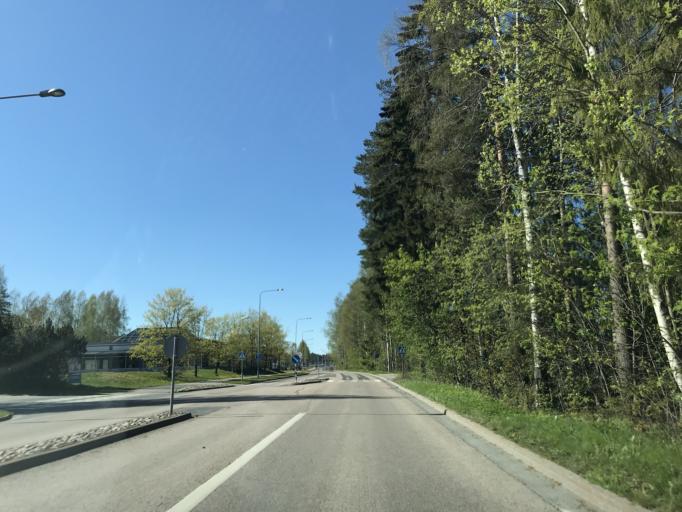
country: FI
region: Uusimaa
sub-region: Helsinki
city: Hyvinge
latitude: 60.6260
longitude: 24.8691
